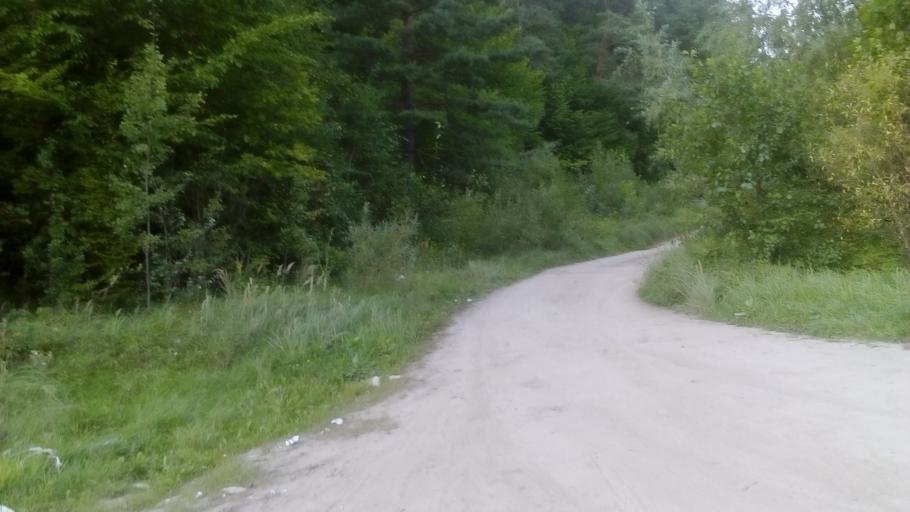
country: LT
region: Alytaus apskritis
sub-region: Alytus
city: Alytus
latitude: 54.4221
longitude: 24.0385
